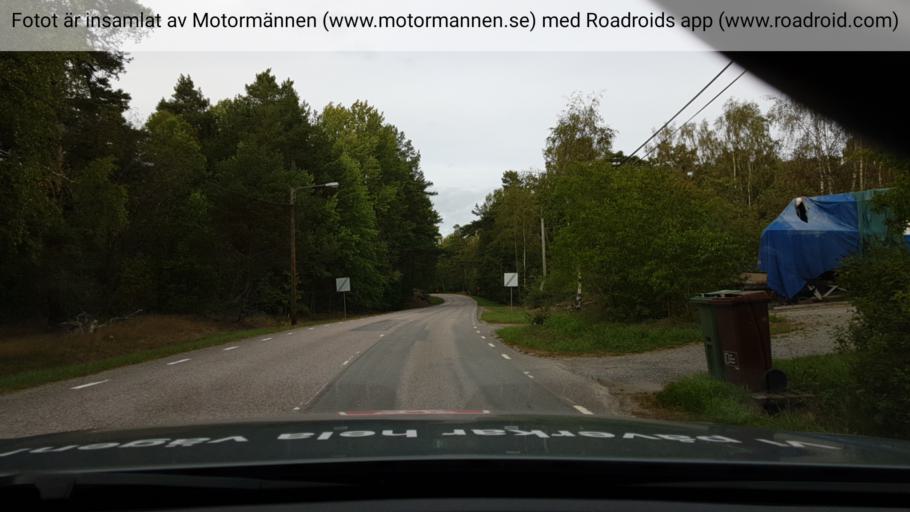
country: SE
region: Stockholm
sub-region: Haninge Kommun
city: Haninge
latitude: 59.0893
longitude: 18.1790
